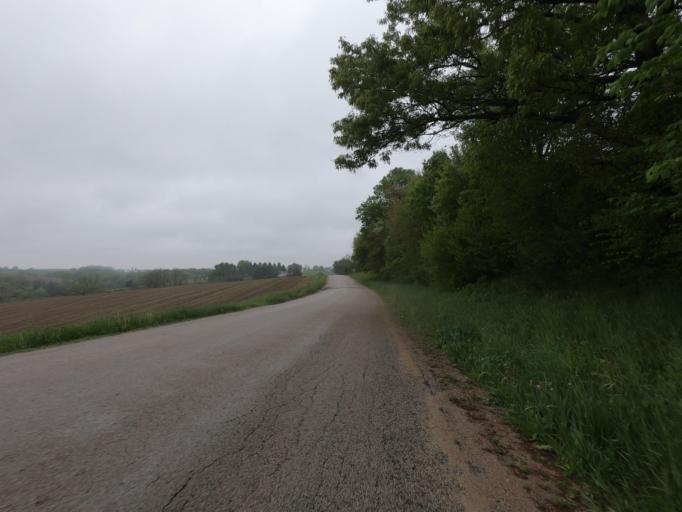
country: US
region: Wisconsin
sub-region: Grant County
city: Hazel Green
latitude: 42.4885
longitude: -90.4925
